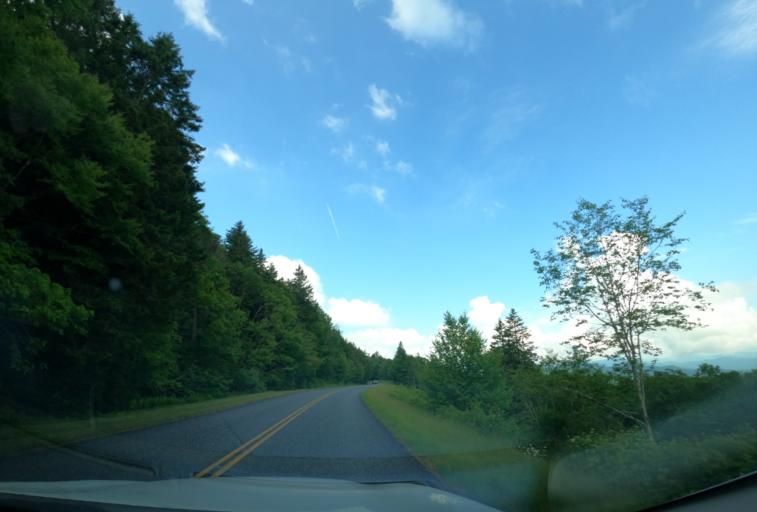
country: US
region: North Carolina
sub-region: Haywood County
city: Hazelwood
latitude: 35.3791
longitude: -83.0097
